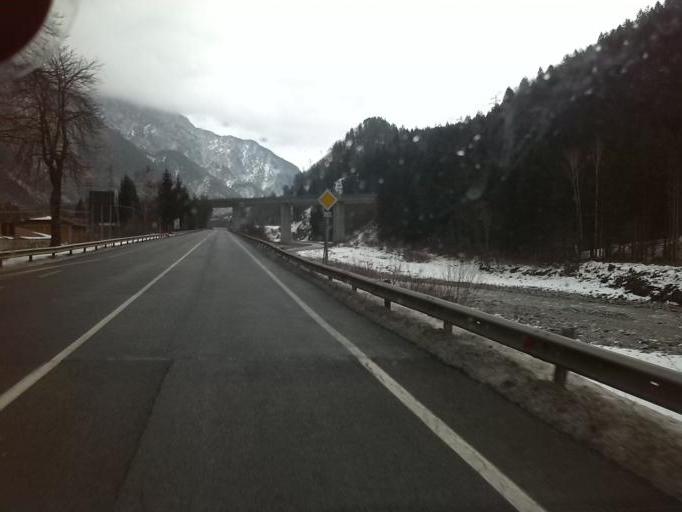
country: IT
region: Friuli Venezia Giulia
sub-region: Provincia di Udine
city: Pontebba
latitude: 46.5085
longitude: 13.3174
